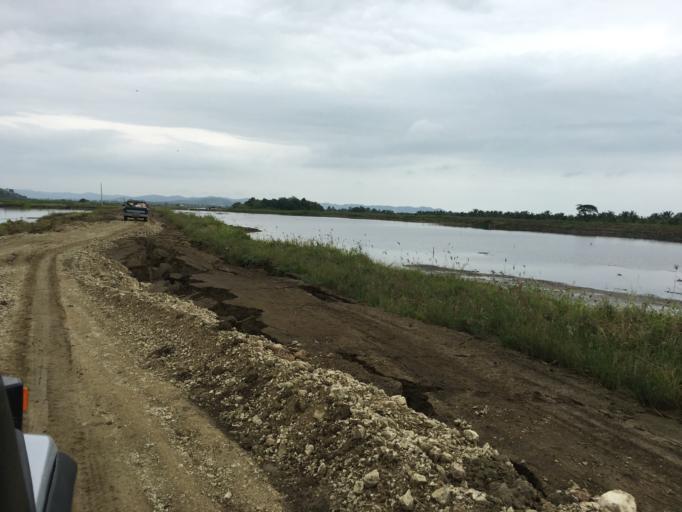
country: EC
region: Manabi
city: Pedernales
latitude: -0.1492
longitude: -80.2434
